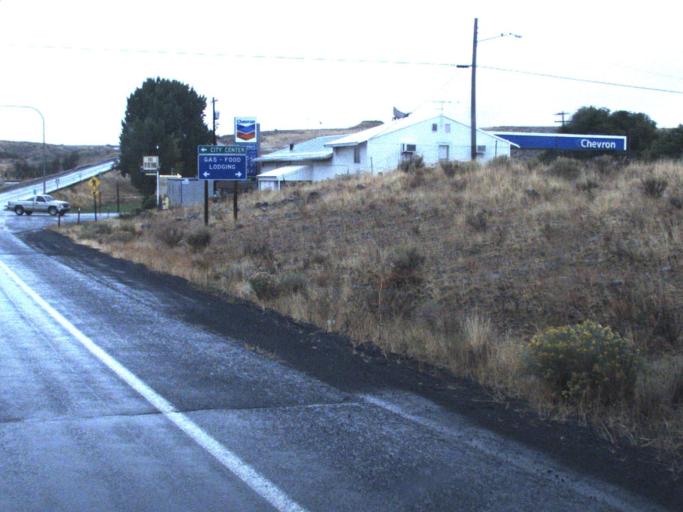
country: US
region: Washington
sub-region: Lincoln County
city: Davenport
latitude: 47.2973
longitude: -117.9739
